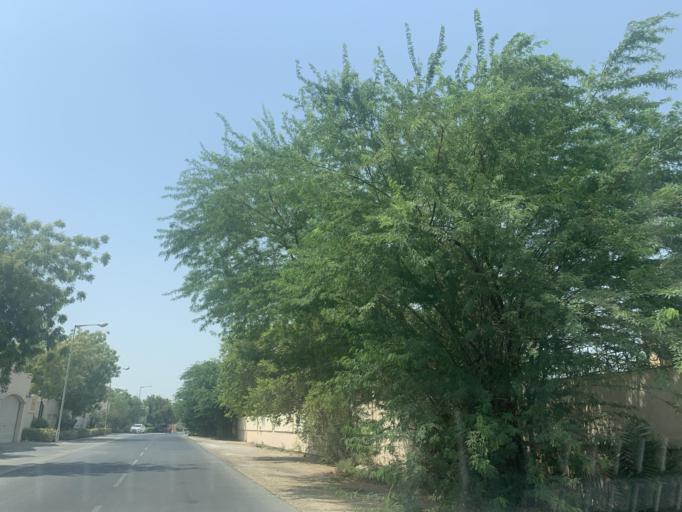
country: BH
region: Manama
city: Jidd Hafs
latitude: 26.2005
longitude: 50.4940
